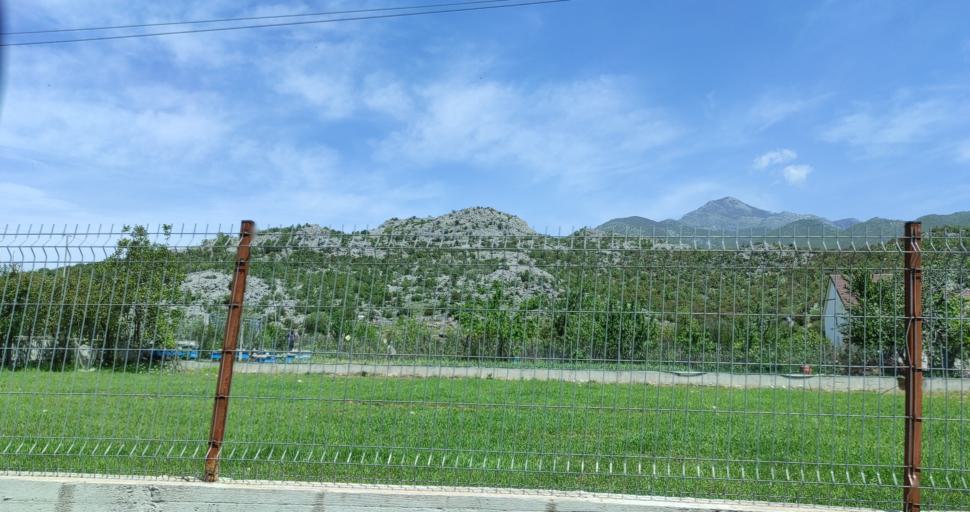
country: AL
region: Shkoder
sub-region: Rrethi i Malesia e Madhe
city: Gruemire
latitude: 42.1479
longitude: 19.5403
